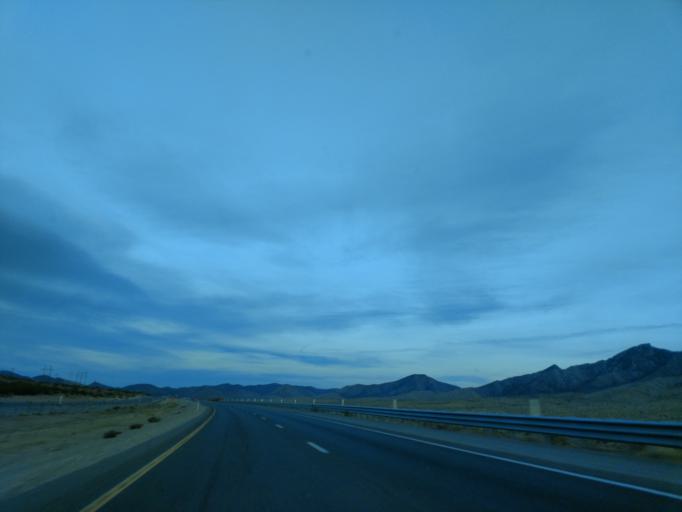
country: US
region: Nevada
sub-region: Clark County
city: Sandy Valley
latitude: 36.0077
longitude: -115.5856
